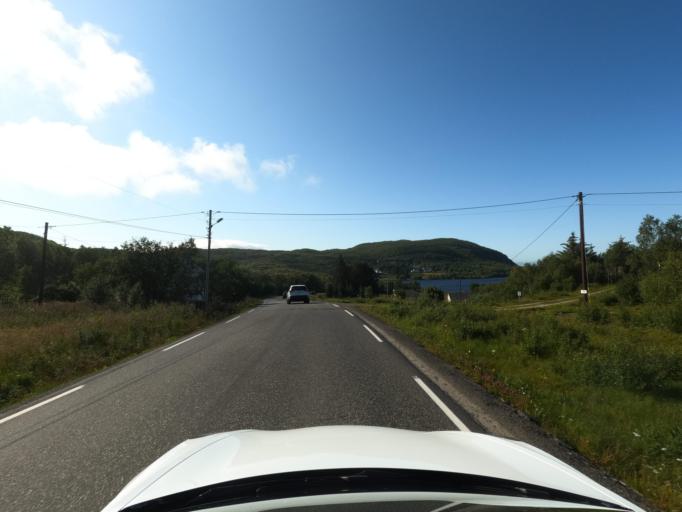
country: NO
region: Nordland
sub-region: Vestvagoy
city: Evjen
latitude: 68.2893
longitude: 13.8780
